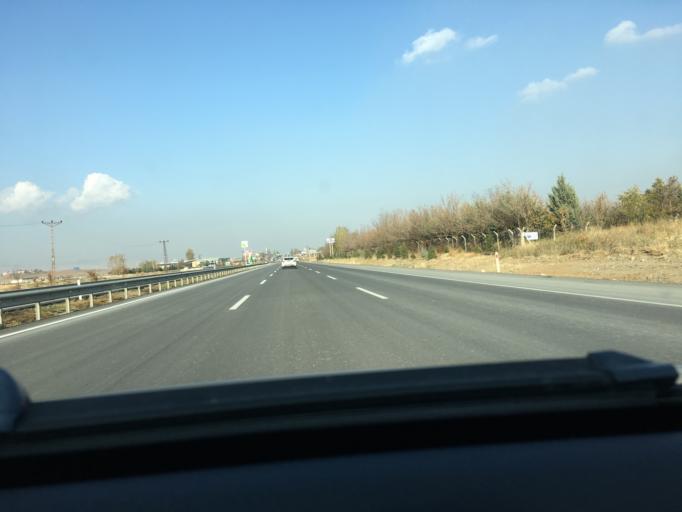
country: TR
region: Ankara
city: Polatli
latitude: 39.6562
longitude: 32.2184
